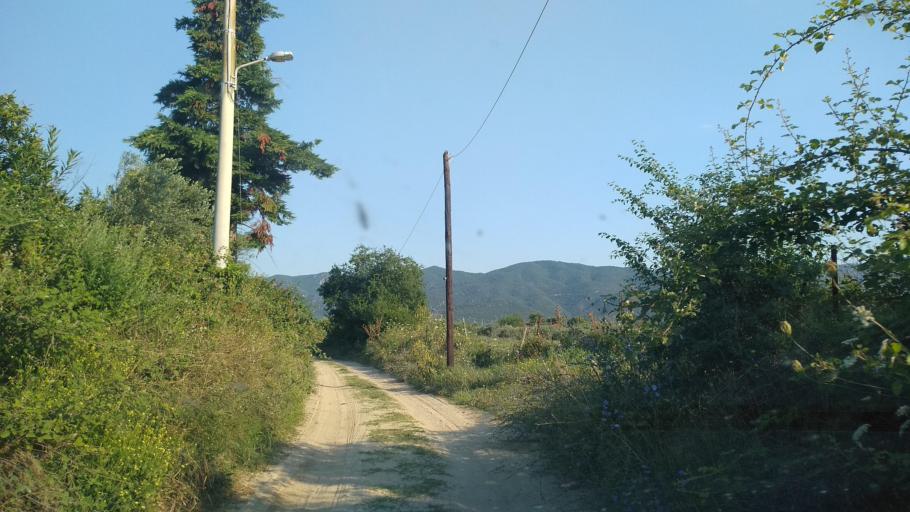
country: GR
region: Central Macedonia
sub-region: Nomos Thessalonikis
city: Nea Vrasna
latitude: 40.6872
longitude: 23.6841
